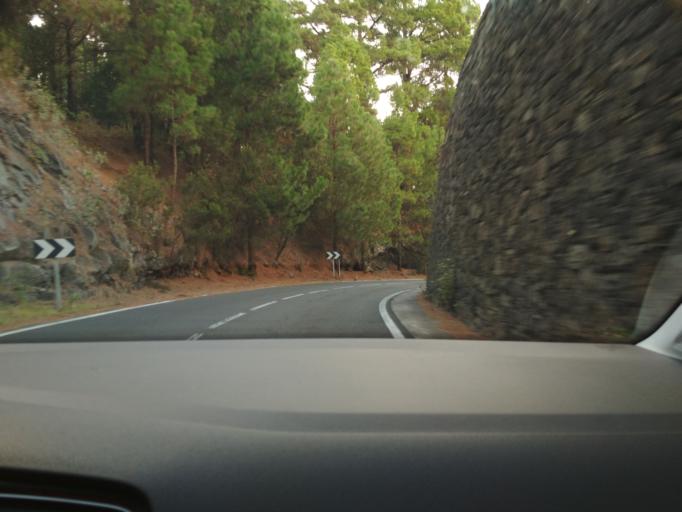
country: ES
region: Canary Islands
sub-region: Provincia de Santa Cruz de Tenerife
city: Garachico
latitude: 28.3347
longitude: -16.7591
